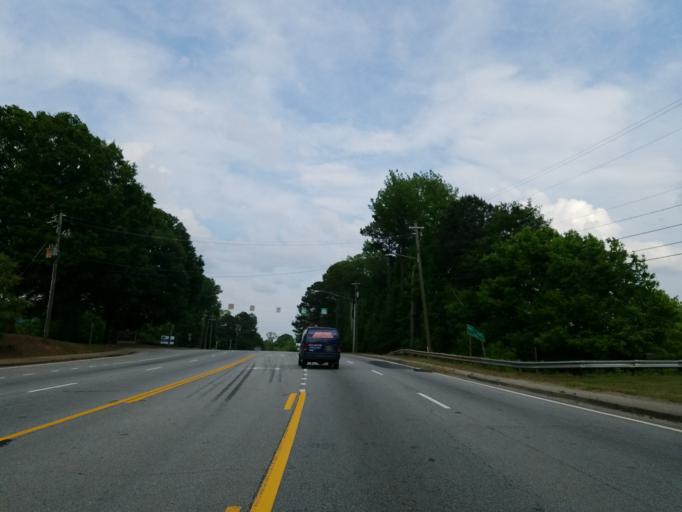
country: US
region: Georgia
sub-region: Cobb County
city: Mableton
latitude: 33.7944
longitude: -84.5049
